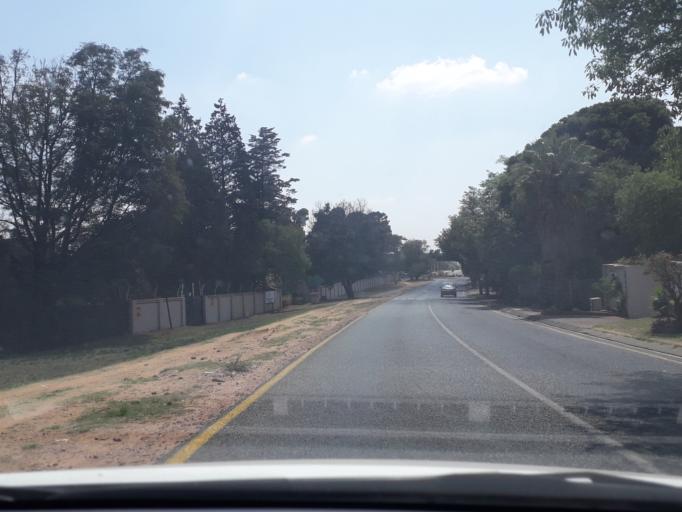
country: ZA
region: Gauteng
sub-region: West Rand District Municipality
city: Muldersdriseloop
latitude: -26.0760
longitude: 27.9299
